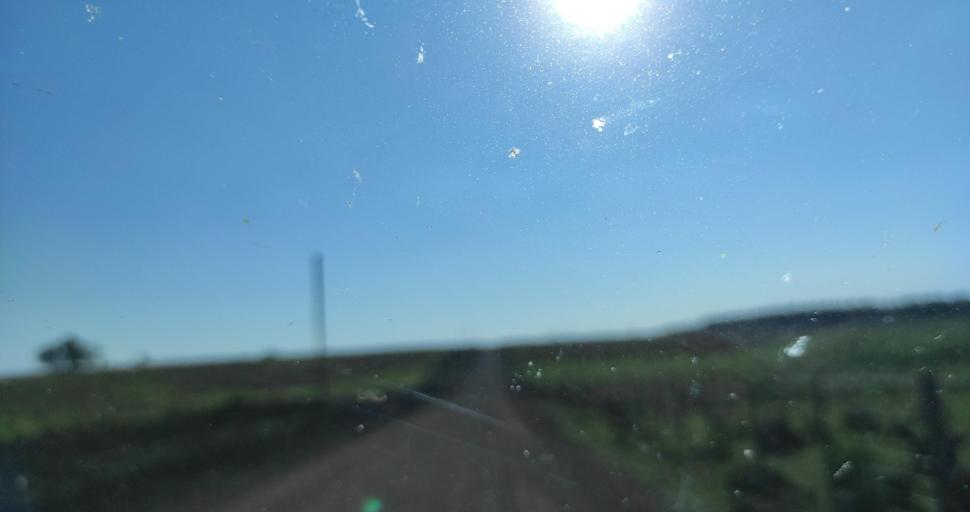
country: PY
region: Itapua
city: San Juan del Parana
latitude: -27.4164
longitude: -56.1301
